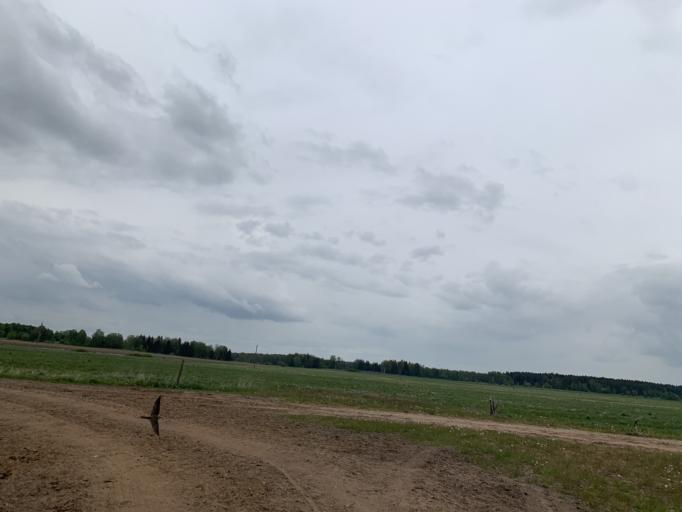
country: BY
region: Minsk
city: Kapyl'
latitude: 53.2483
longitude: 26.9489
